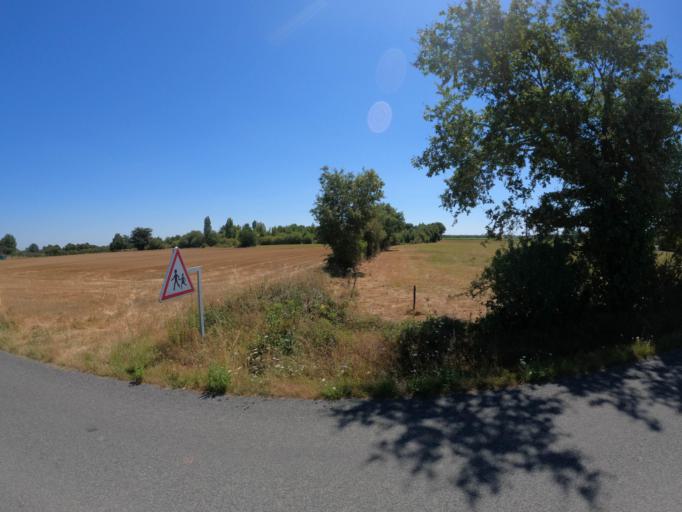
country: FR
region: Pays de la Loire
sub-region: Departement de la Vendee
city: Saint-Philbert-de-Bouaine
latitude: 46.9756
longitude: -1.5471
